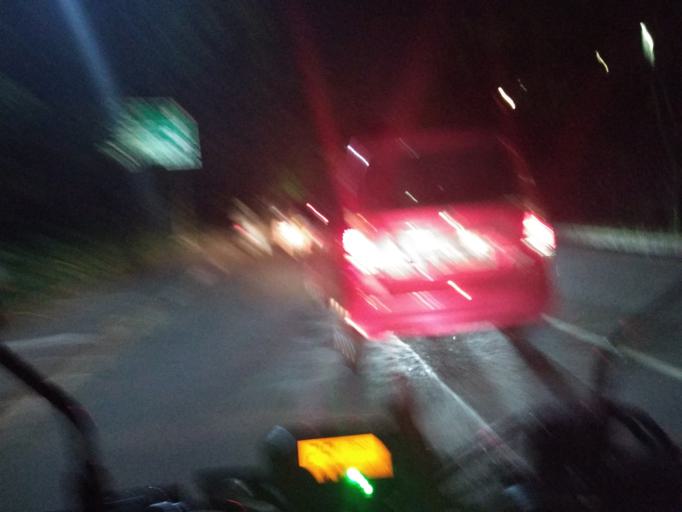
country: ID
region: West Java
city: Bogor
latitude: -6.5900
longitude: 106.8016
